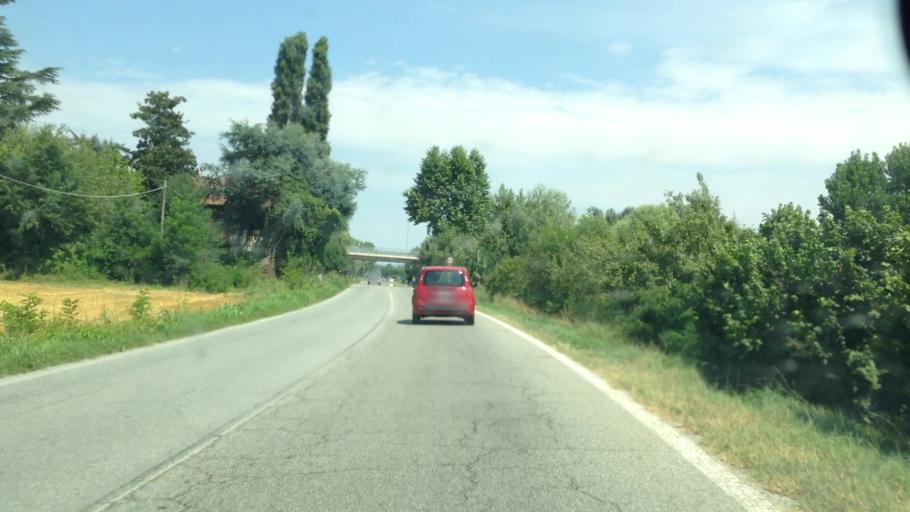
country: IT
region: Piedmont
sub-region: Provincia di Asti
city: Asti
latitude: 44.9216
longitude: 8.2263
